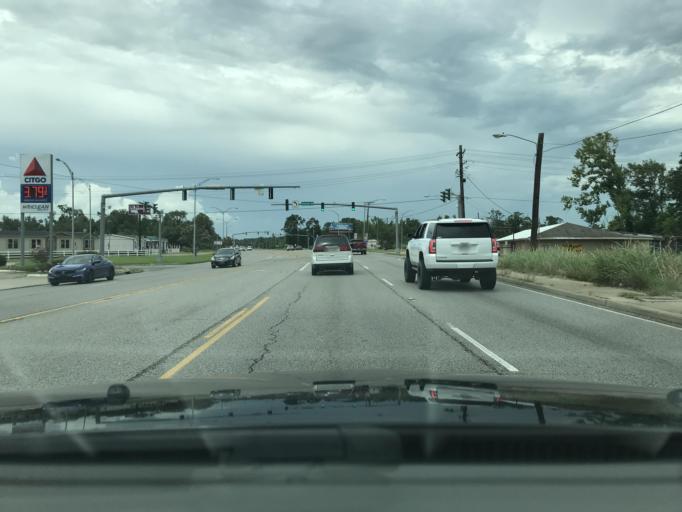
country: US
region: Louisiana
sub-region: Calcasieu Parish
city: Moss Bluff
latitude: 30.2636
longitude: -93.1806
